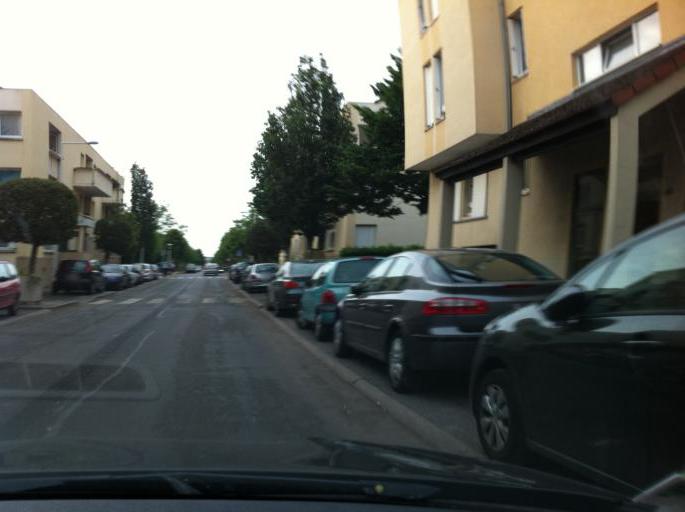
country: FR
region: Ile-de-France
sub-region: Departement de Seine-et-Marne
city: Moissy-Cramayel
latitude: 48.6260
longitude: 2.5804
